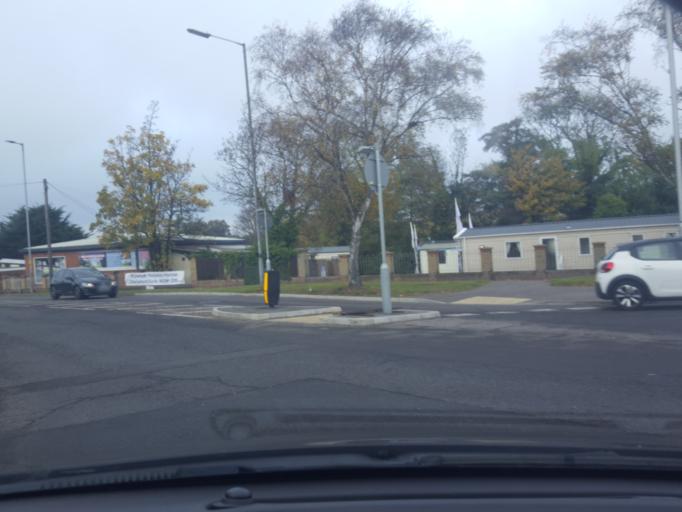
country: GB
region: England
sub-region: Essex
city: Clacton-on-Sea
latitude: 51.8020
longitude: 1.1715
